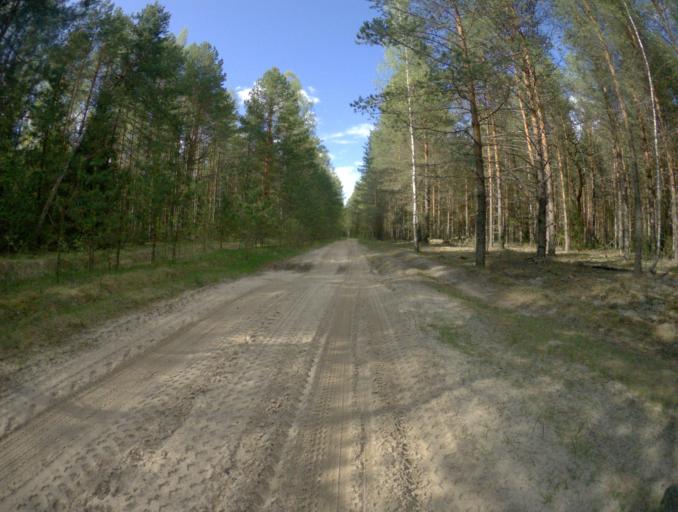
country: RU
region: Vladimir
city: Golovino
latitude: 55.9073
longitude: 40.4426
